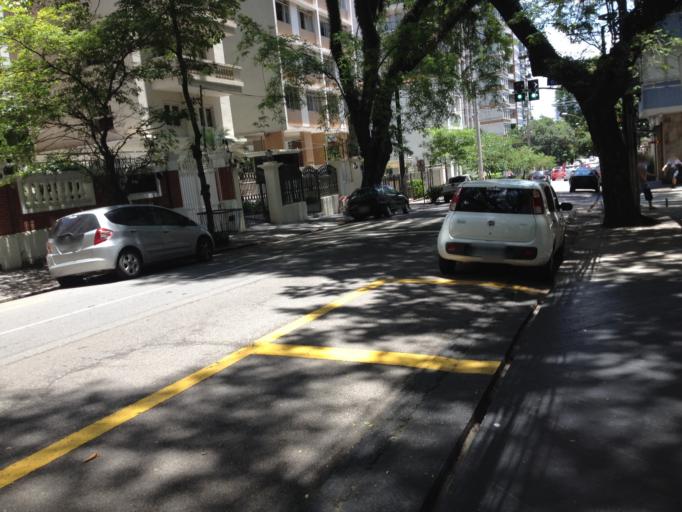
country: BR
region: Sao Paulo
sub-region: Sao Paulo
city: Sao Paulo
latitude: -23.5685
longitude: -46.6625
